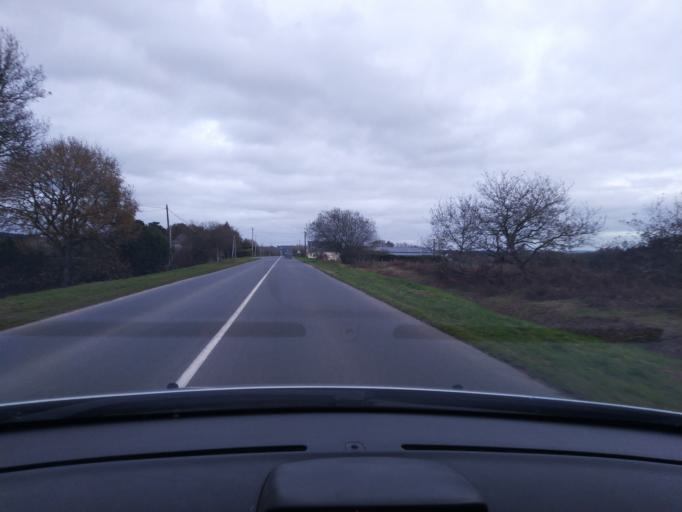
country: FR
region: Brittany
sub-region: Departement du Finistere
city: Guerlesquin
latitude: 48.5651
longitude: -3.5305
